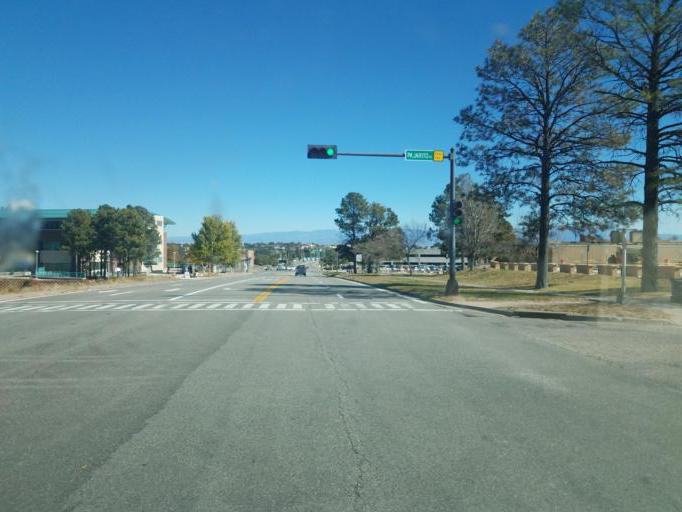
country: US
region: New Mexico
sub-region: Los Alamos County
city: Los Alamos
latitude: 35.8765
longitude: -106.3265
